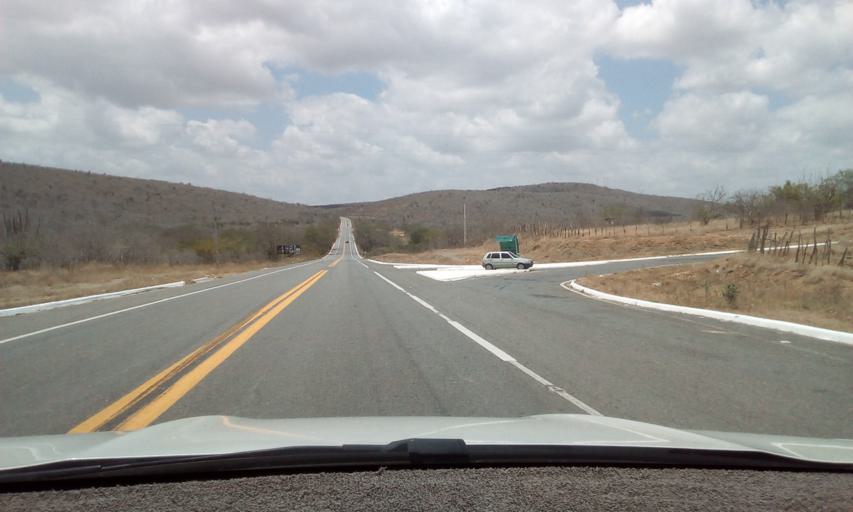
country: BR
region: Paraiba
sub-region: Boqueirao
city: Boqueirao
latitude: -7.6594
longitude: -36.0797
